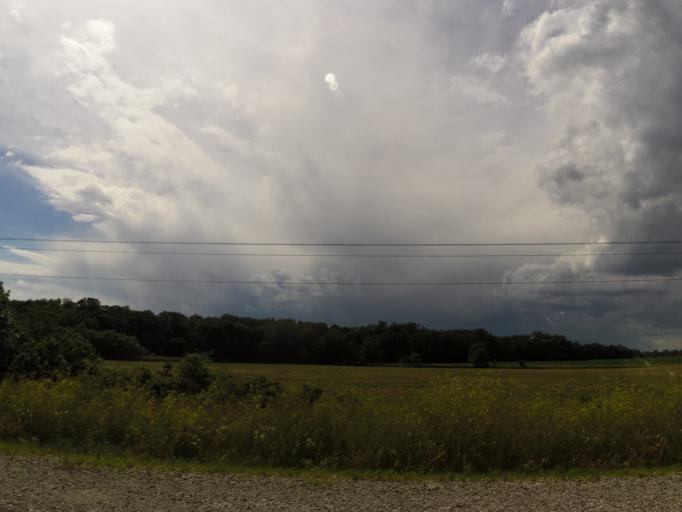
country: US
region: Iowa
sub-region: Henry County
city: Winfield
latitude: 41.1813
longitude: -91.5358
